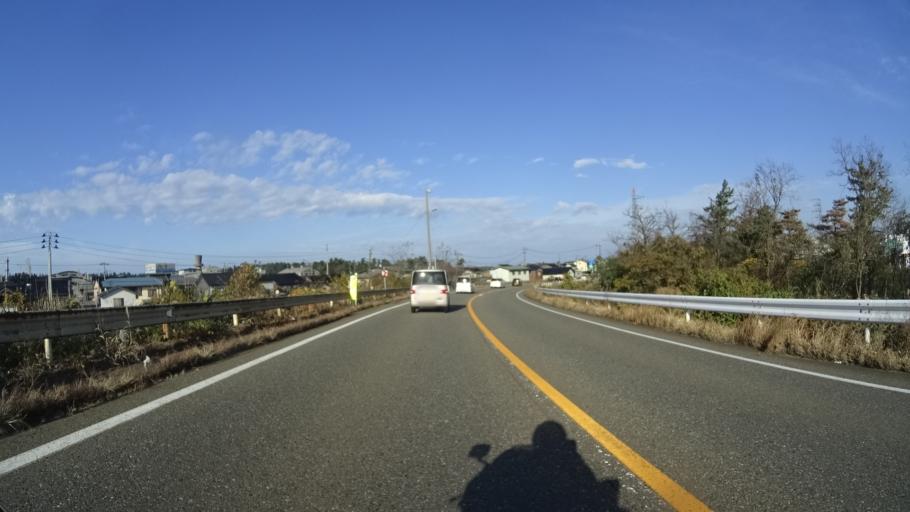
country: JP
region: Niigata
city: Joetsu
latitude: 37.2079
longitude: 138.3005
